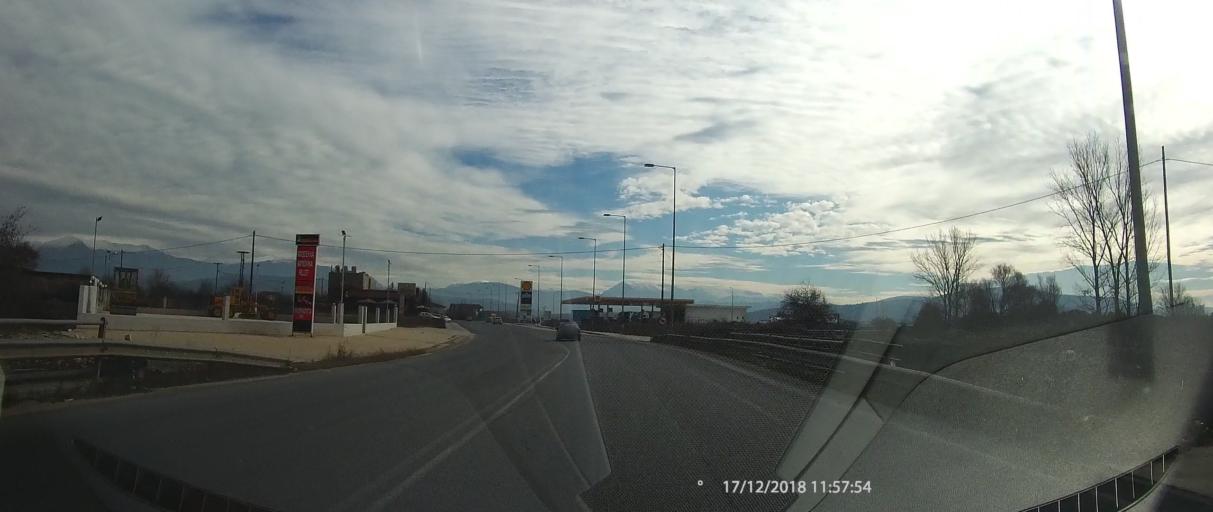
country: GR
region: Epirus
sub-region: Nomos Ioanninon
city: Neochoropoulo
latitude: 39.6229
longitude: 20.8530
